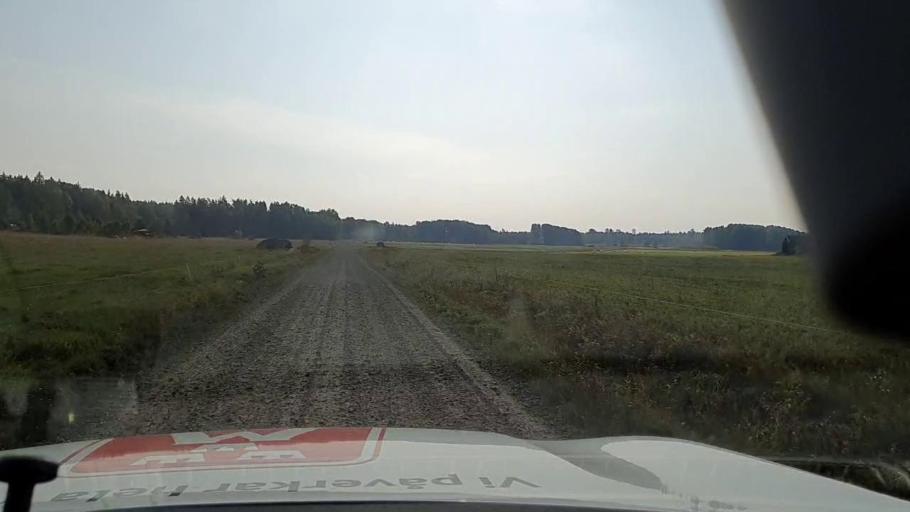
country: SE
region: Vaestmanland
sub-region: Kungsors Kommun
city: Kungsoer
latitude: 59.3545
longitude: 16.1592
